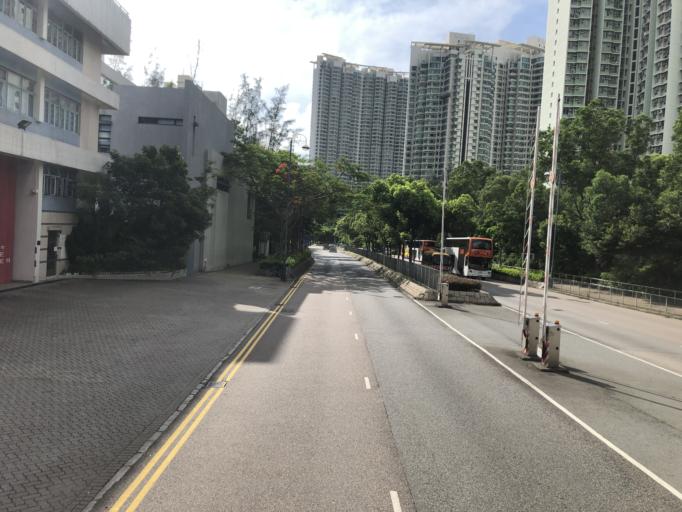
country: HK
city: Tai O
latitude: 22.2853
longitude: 113.9420
